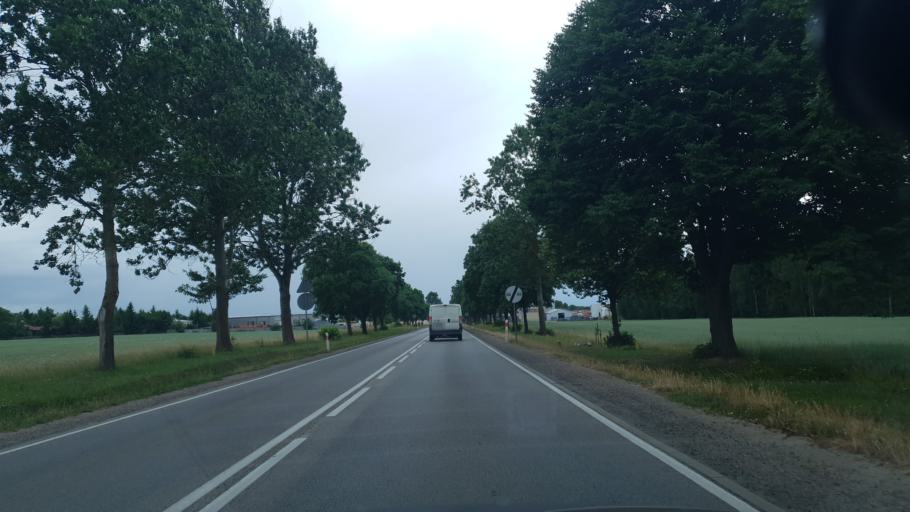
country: PL
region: Pomeranian Voivodeship
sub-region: Powiat kartuski
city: Banino
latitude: 54.4087
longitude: 18.3688
